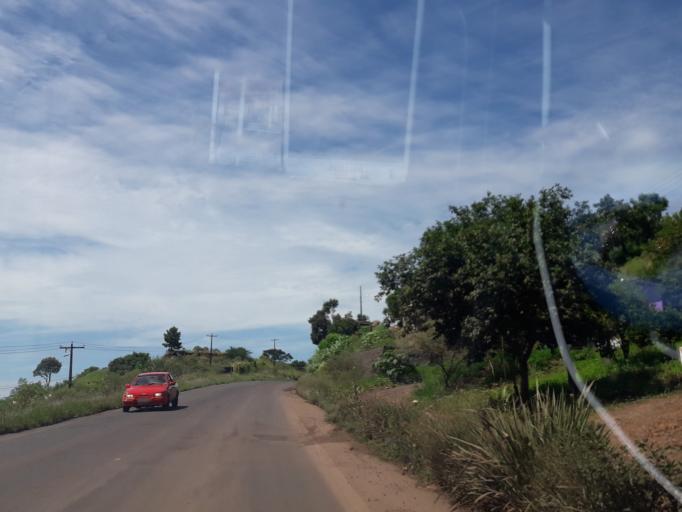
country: AR
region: Misiones
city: Bernardo de Irigoyen
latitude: -26.6076
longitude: -53.5171
